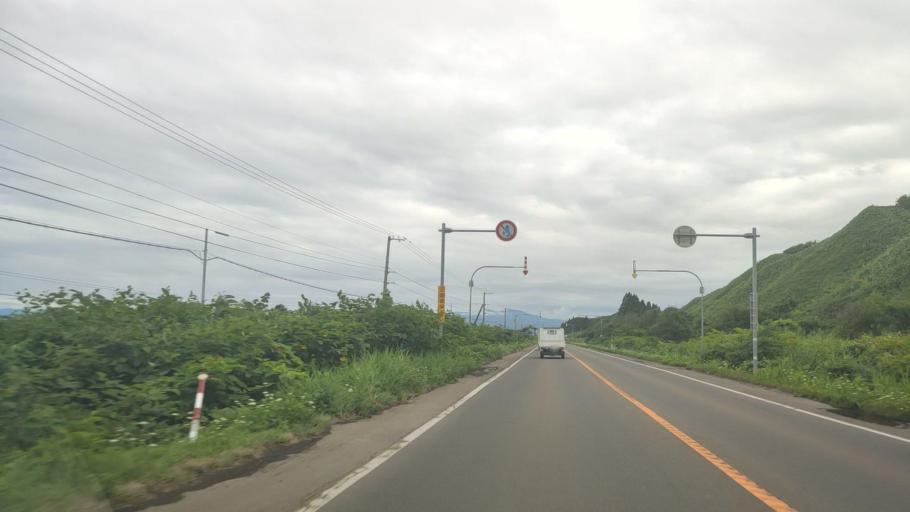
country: JP
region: Hokkaido
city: Niseko Town
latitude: 42.3488
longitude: 140.2831
